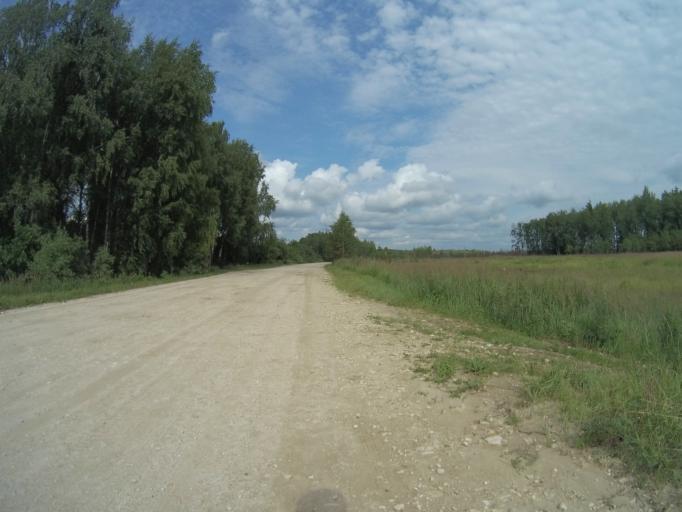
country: RU
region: Vladimir
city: Orgtrud
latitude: 56.2448
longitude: 40.6915
